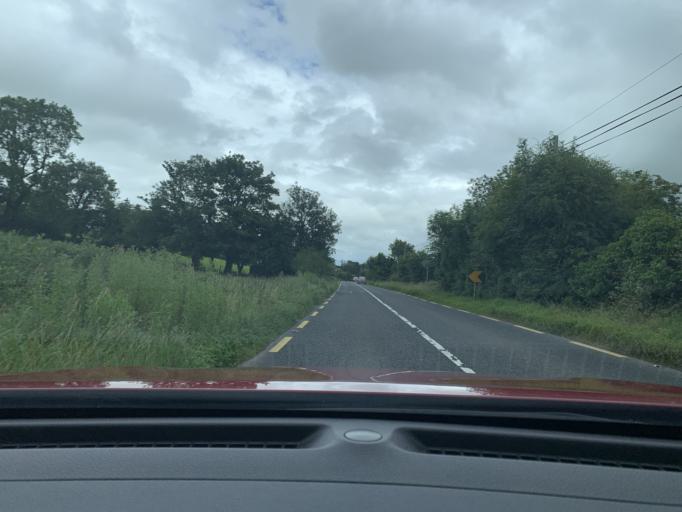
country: IE
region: Ulster
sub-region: County Donegal
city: Convoy
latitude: 54.8012
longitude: -7.6208
